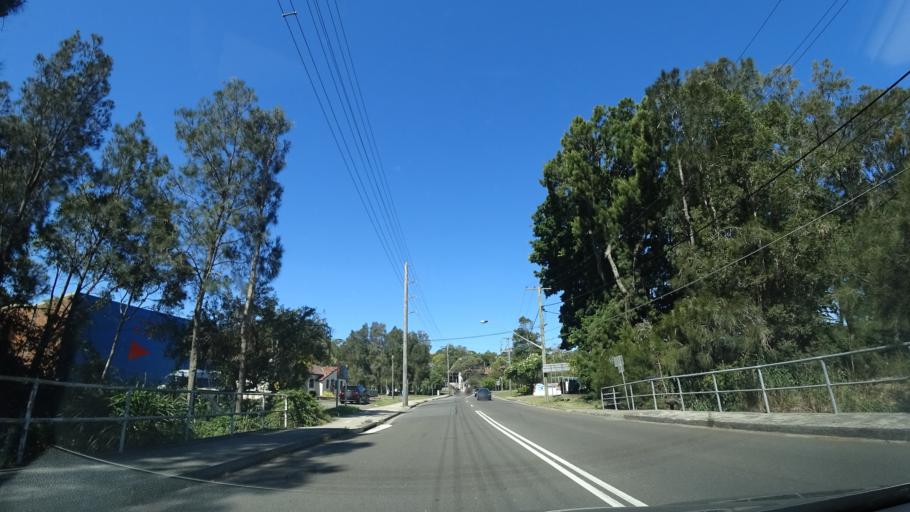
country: AU
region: New South Wales
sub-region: Warringah
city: North Manly
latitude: -33.7757
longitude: 151.2692
